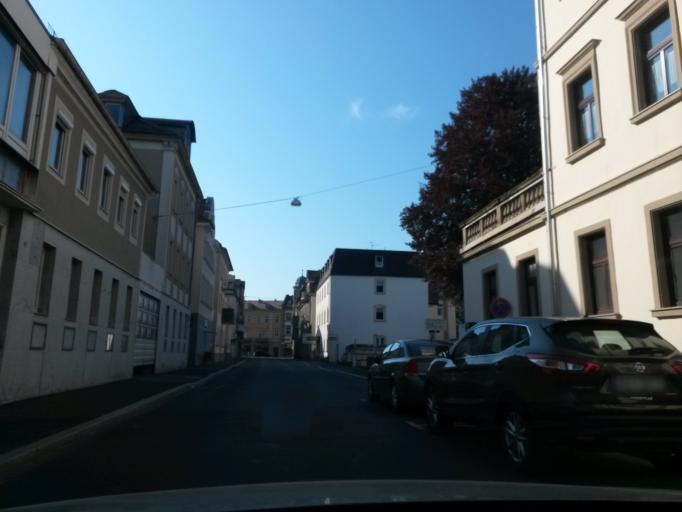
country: DE
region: Bavaria
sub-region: Regierungsbezirk Unterfranken
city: Bad Kissingen
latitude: 50.1997
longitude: 10.0745
